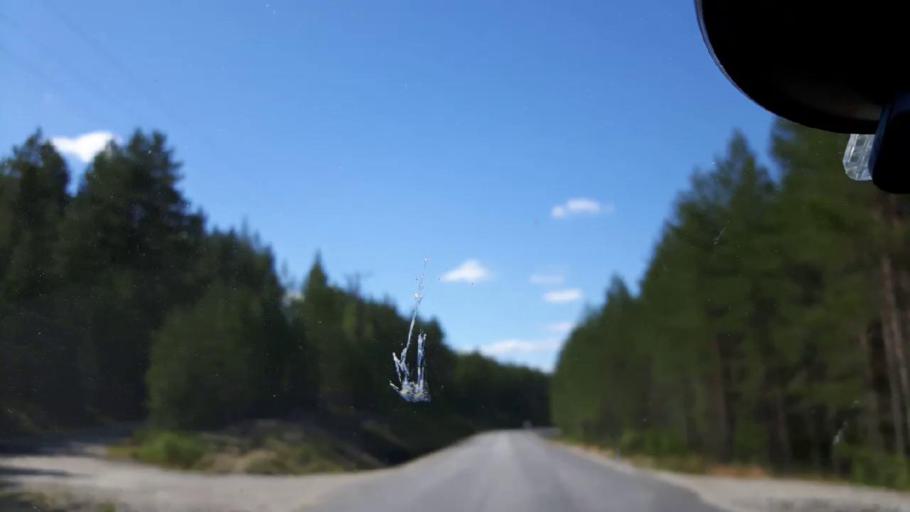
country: SE
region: Vaesternorrland
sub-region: Ange Kommun
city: Fransta
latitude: 62.7013
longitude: 16.3839
